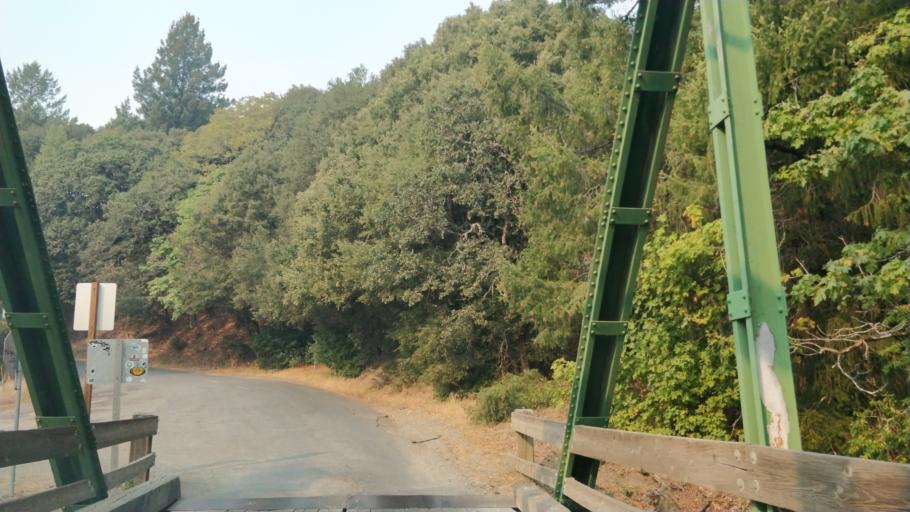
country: US
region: California
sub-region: Humboldt County
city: Rio Dell
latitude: 40.2443
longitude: -124.1228
